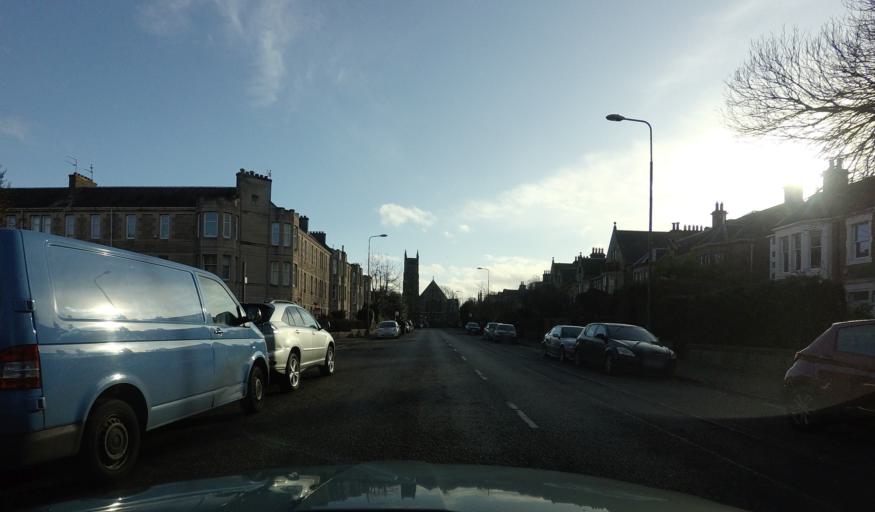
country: GB
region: Scotland
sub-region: Edinburgh
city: Edinburgh
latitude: 55.9720
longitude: -3.2145
